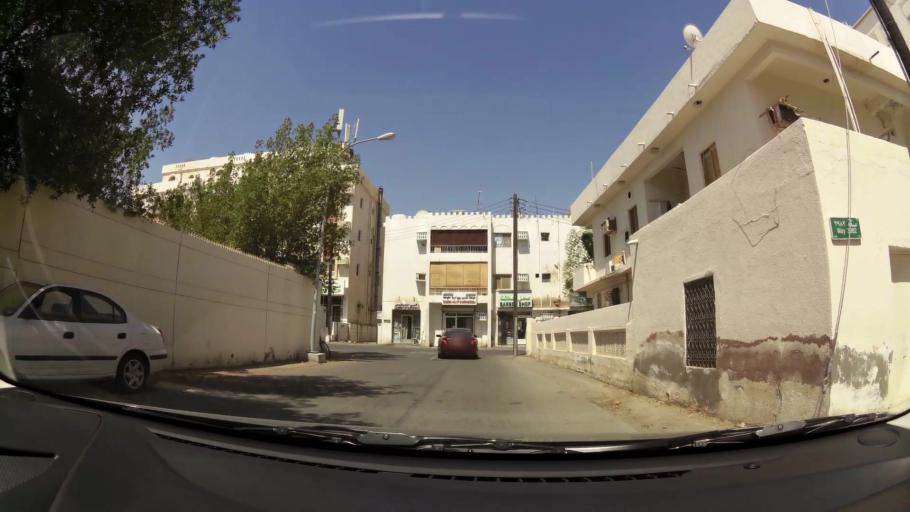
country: OM
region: Muhafazat Masqat
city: Muscat
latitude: 23.5984
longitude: 58.5439
